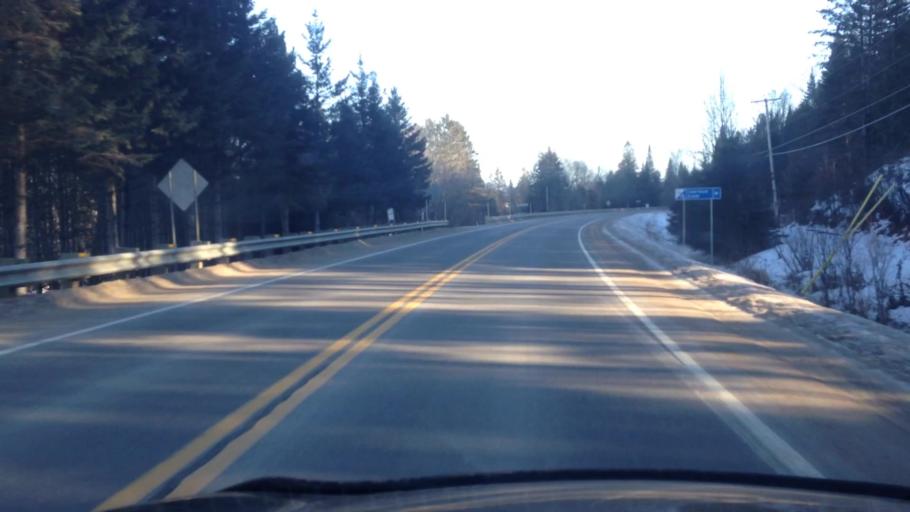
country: CA
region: Quebec
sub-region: Laurentides
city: Mont-Tremblant
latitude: 45.9655
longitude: -74.6129
